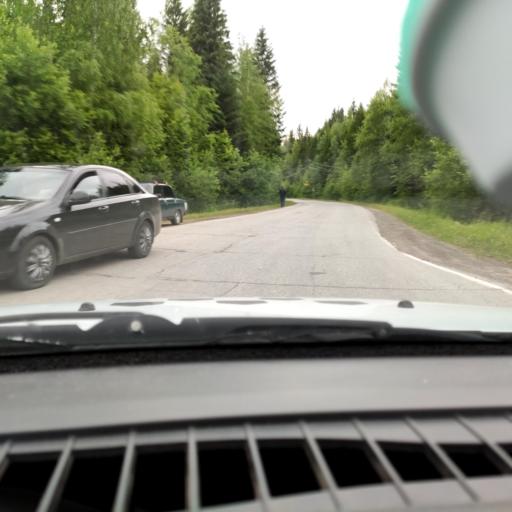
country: RU
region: Perm
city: Lys'va
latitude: 58.1138
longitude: 57.7028
